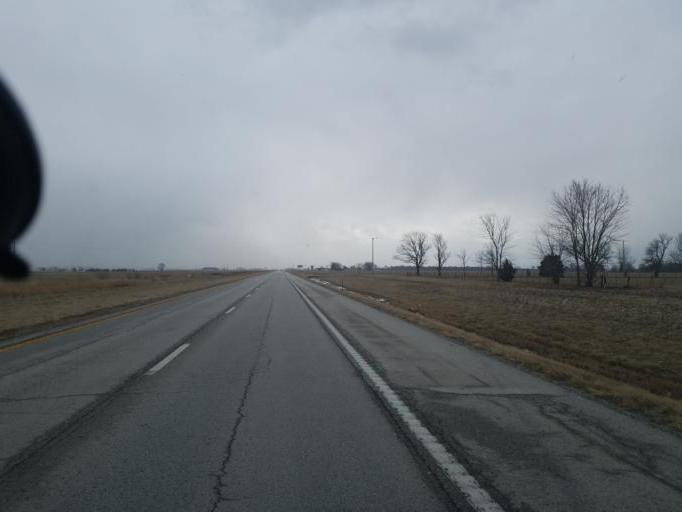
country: US
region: Missouri
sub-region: Randolph County
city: Huntsville
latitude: 39.5707
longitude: -92.4646
